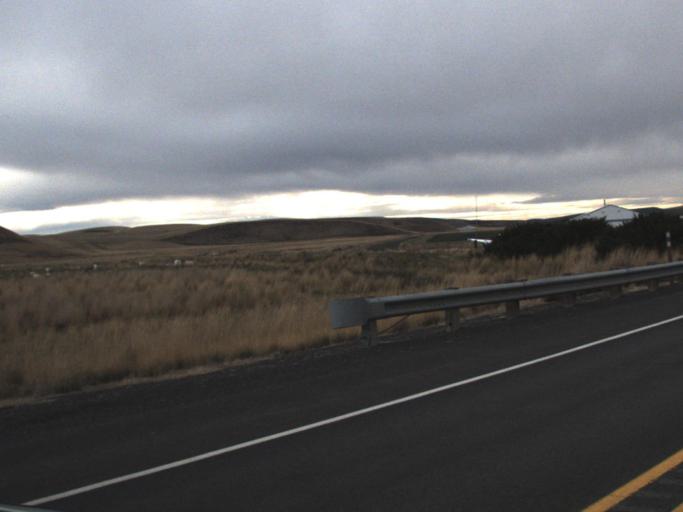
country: US
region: Washington
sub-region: Whitman County
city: Colfax
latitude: 46.8090
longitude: -117.6488
